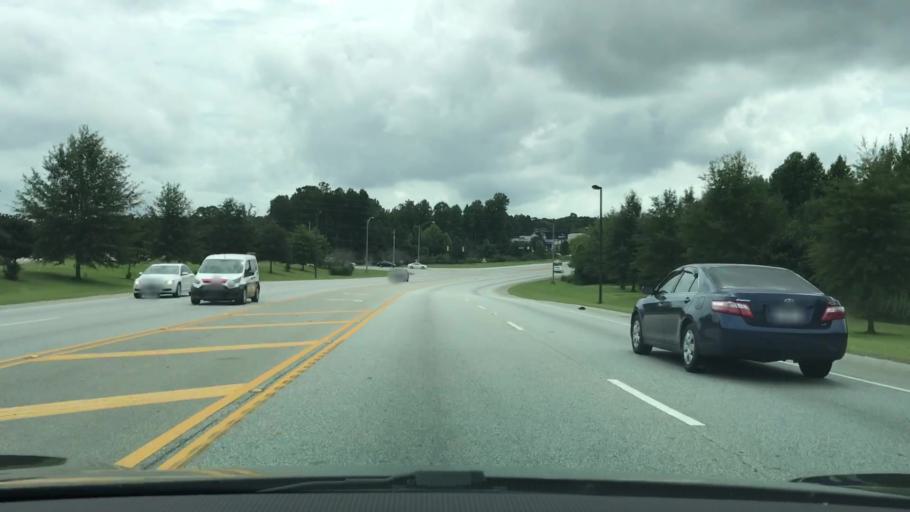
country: US
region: Alabama
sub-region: Lee County
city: Opelika
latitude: 32.6309
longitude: -85.4072
